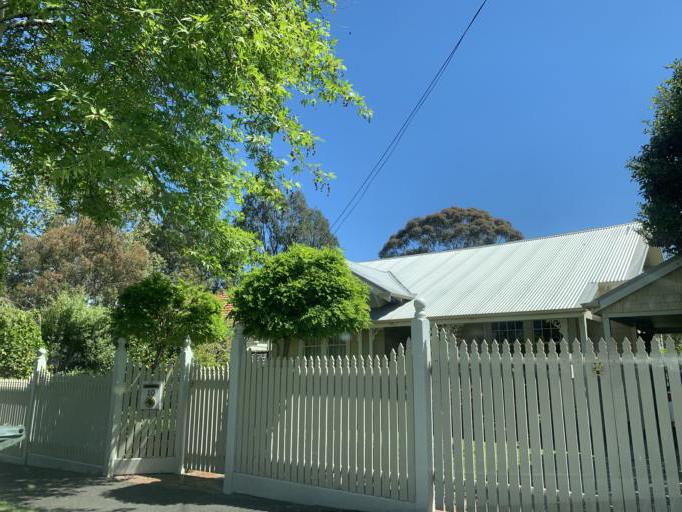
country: AU
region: Victoria
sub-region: Bayside
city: Brighton East
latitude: -37.9093
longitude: 145.0143
